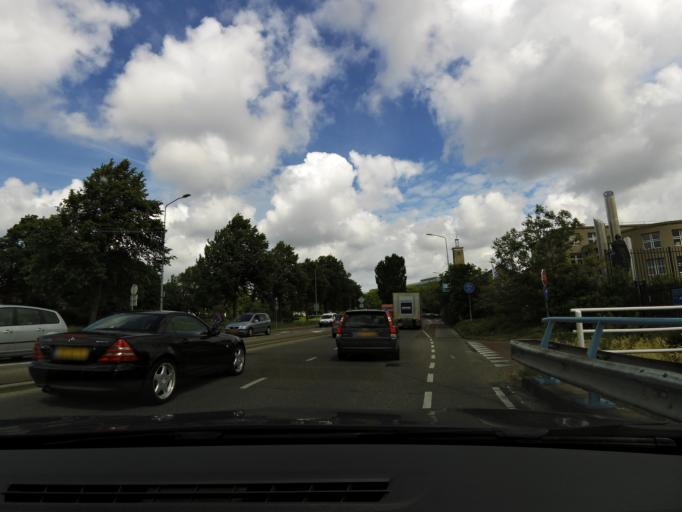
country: NL
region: Zeeland
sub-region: Gemeente Middelburg
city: Middelburg
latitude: 51.4935
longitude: 3.6072
